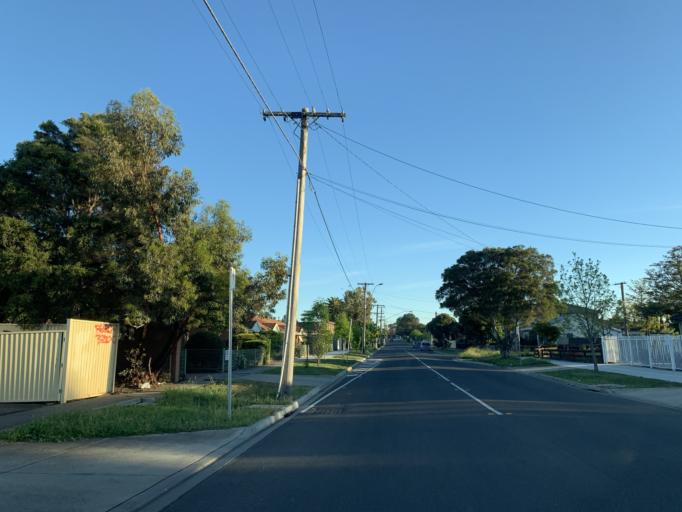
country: AU
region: Victoria
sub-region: Brimbank
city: St Albans
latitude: -37.7485
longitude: 144.8039
